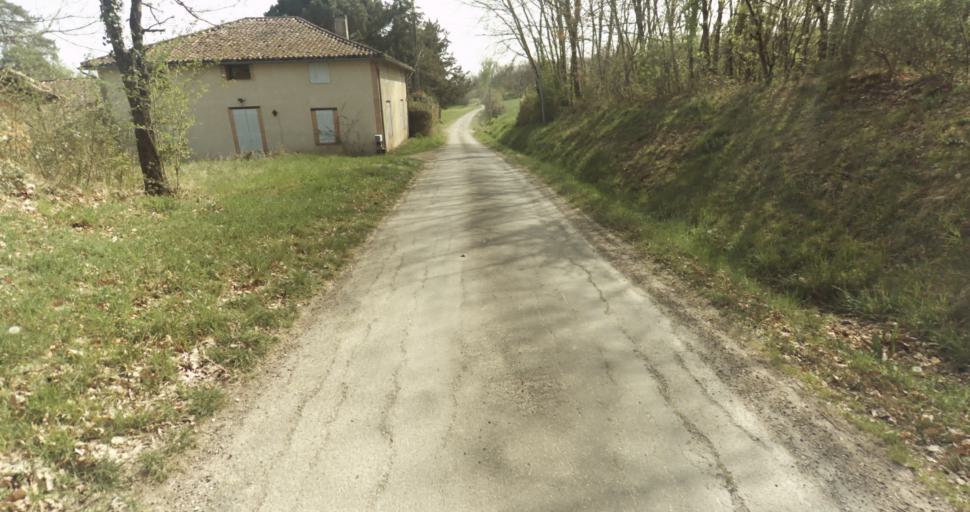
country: FR
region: Midi-Pyrenees
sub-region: Departement du Tarn-et-Garonne
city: Moissac
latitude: 44.1413
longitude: 1.1592
